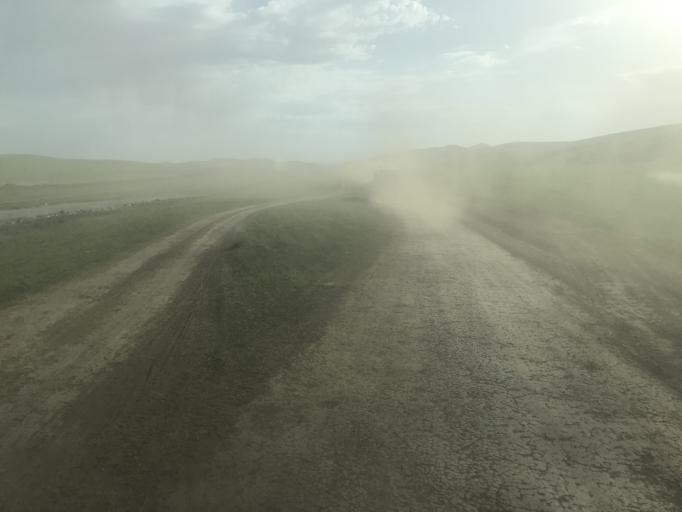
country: MN
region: Central Aimak
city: Javhlant
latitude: 48.6541
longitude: 106.1135
